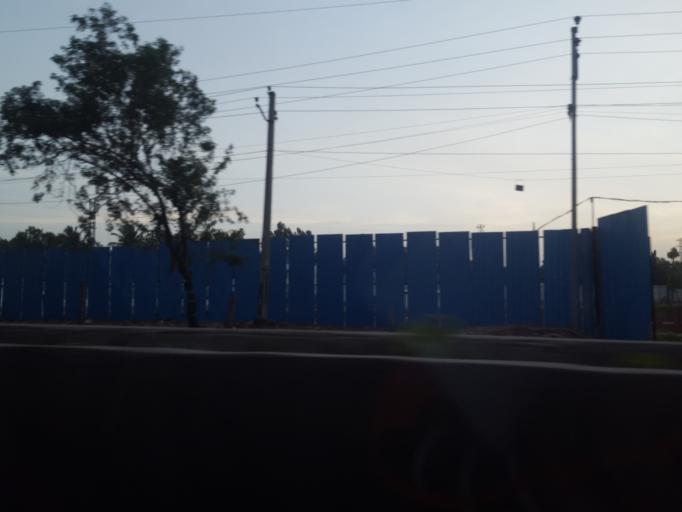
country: IN
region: Telangana
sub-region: Medak
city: Serilingampalle
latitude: 17.5232
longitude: 78.3562
